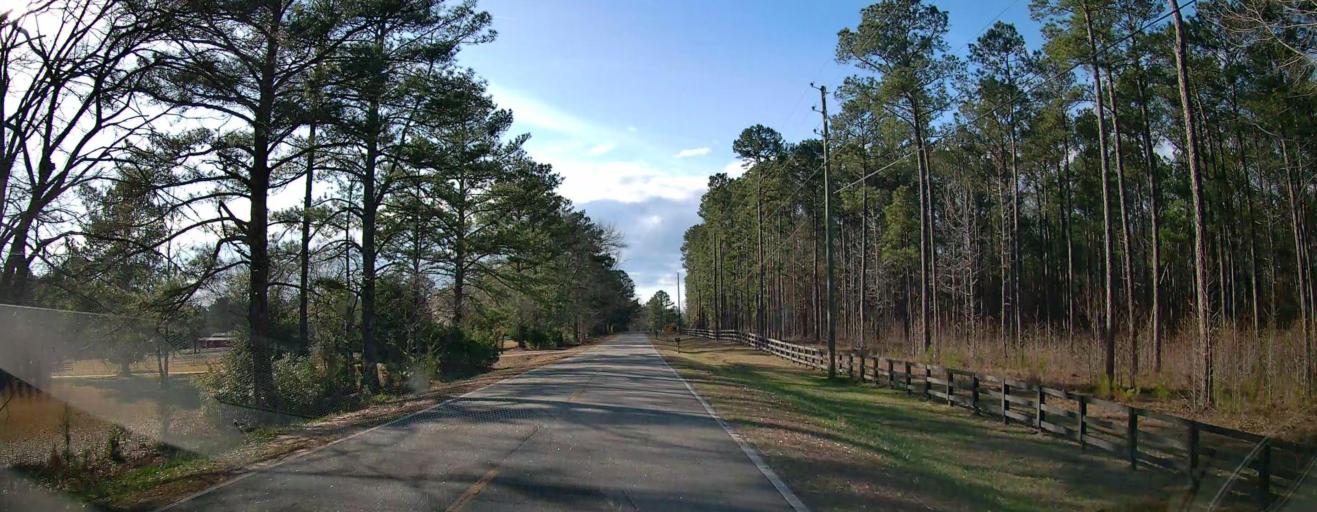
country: US
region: Georgia
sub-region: Harris County
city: Hamilton
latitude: 32.5606
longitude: -84.7874
